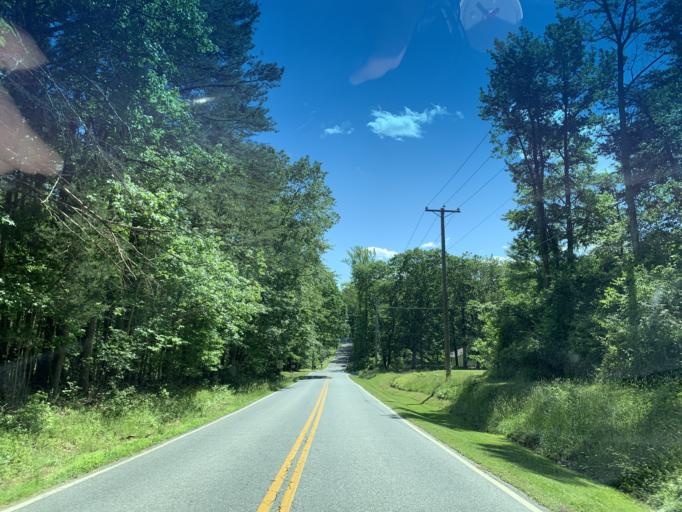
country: US
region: Maryland
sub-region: Cecil County
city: North East
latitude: 39.5425
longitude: -75.9158
